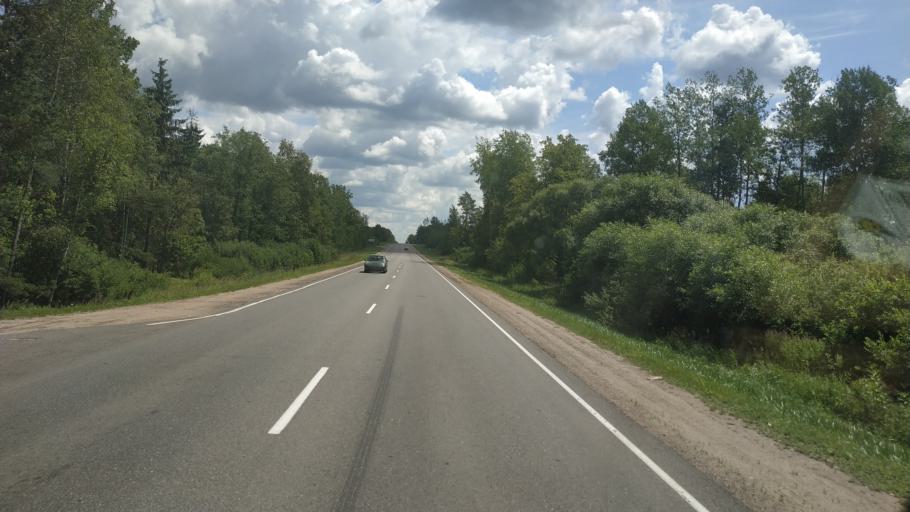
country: BY
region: Mogilev
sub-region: Mahilyowski Rayon
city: Veyno
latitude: 53.8229
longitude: 30.4284
